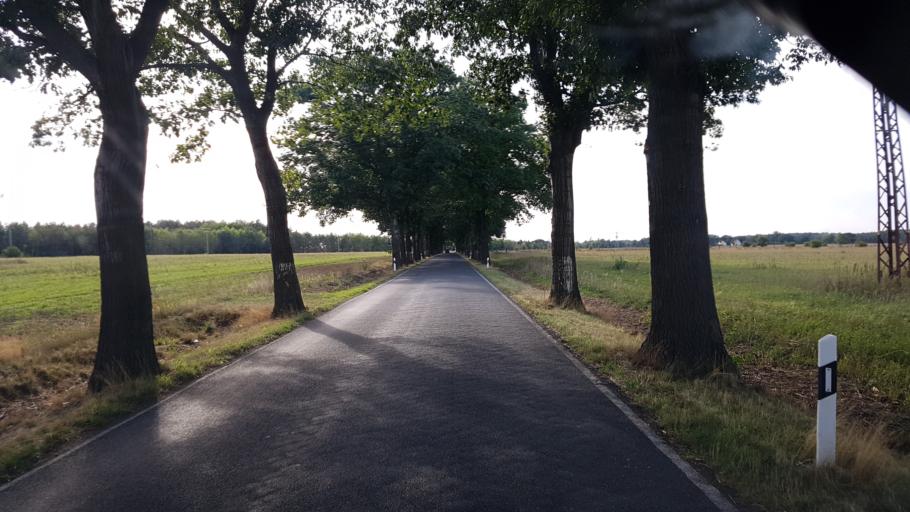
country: DE
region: Brandenburg
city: Welzow
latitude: 51.5565
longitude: 14.1480
